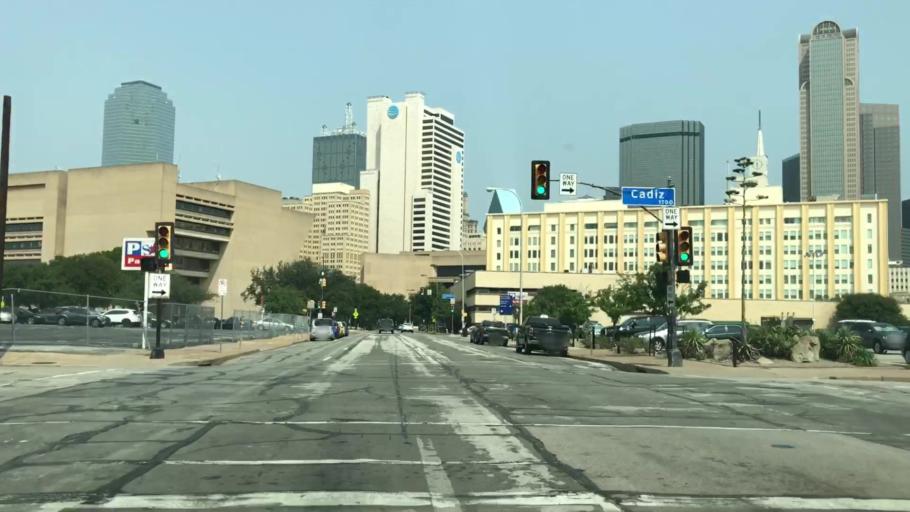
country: US
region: Texas
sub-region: Dallas County
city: Dallas
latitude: 32.7753
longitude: -96.7941
